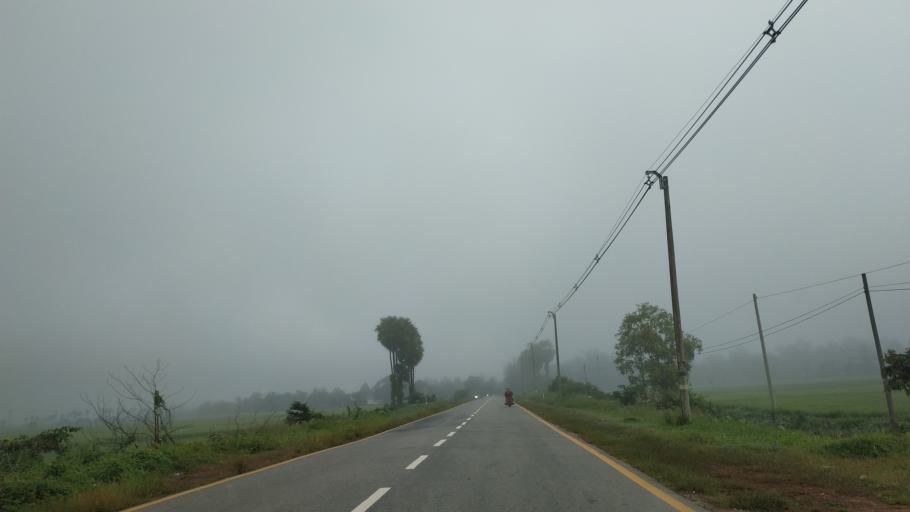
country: MM
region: Tanintharyi
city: Dawei
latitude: 14.1230
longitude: 98.2174
